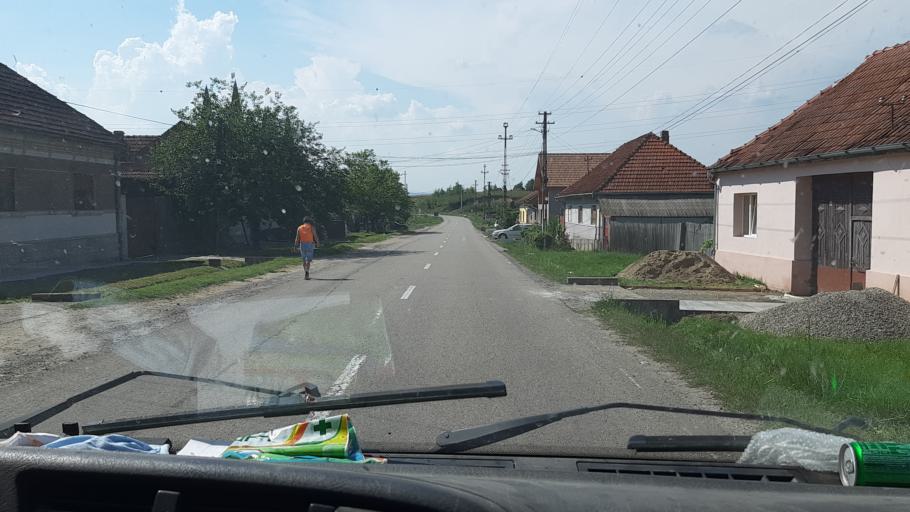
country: RO
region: Caras-Severin
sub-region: Comuna Ezeris
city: Ezeris
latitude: 45.3775
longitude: 21.9399
